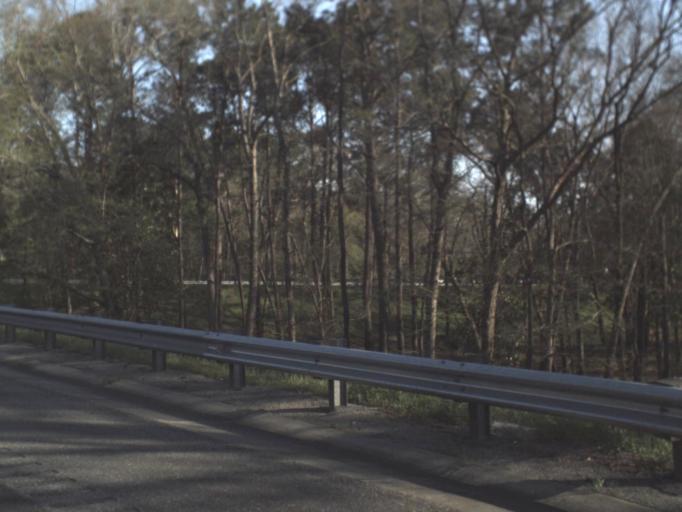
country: US
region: Florida
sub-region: Gadsden County
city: Midway
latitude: 30.4904
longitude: -84.4279
